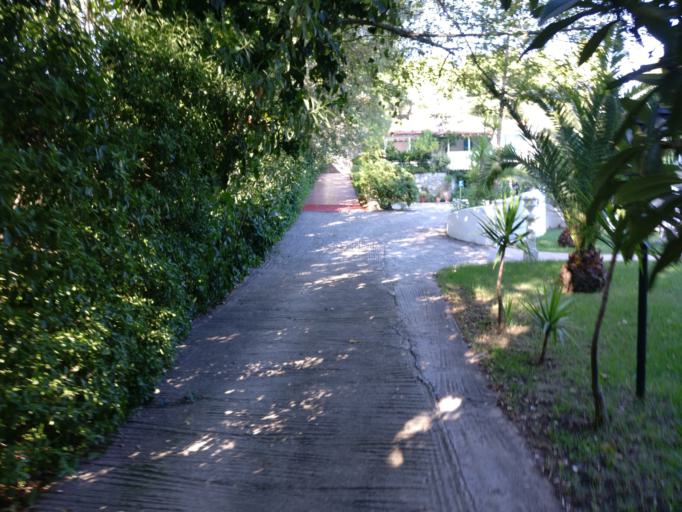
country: GR
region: Thessaly
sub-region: Nomos Magnisias
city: Skiathos
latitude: 39.1527
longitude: 23.4094
